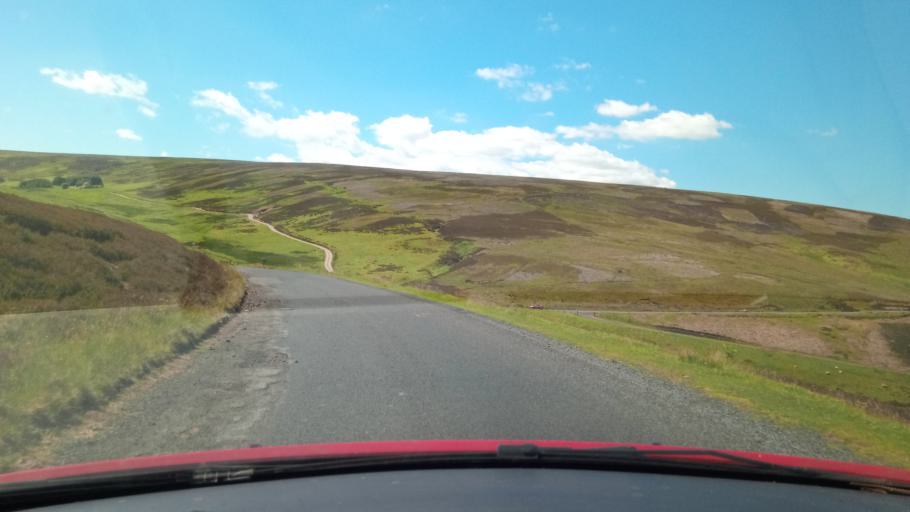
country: GB
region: Scotland
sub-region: East Lothian
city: East Linton
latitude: 55.8432
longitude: -2.5802
